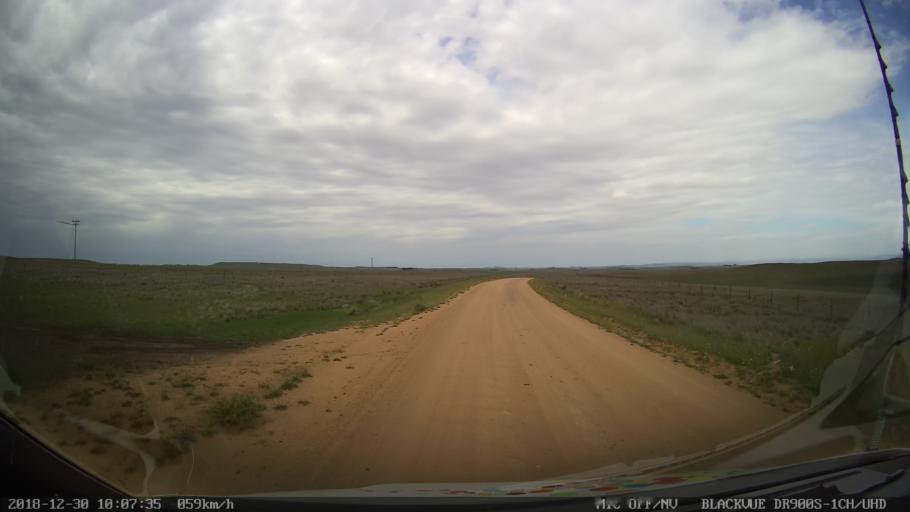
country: AU
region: New South Wales
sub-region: Cooma-Monaro
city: Cooma
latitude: -36.5405
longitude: 149.1217
